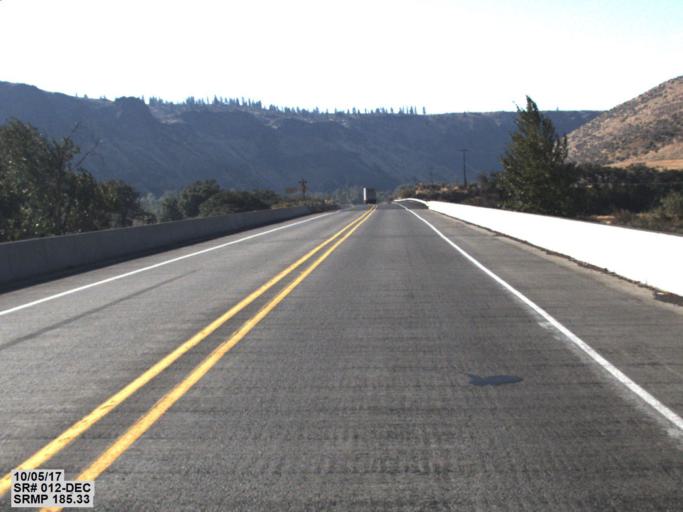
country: US
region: Washington
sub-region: Yakima County
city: Tieton
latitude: 46.7464
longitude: -120.7887
